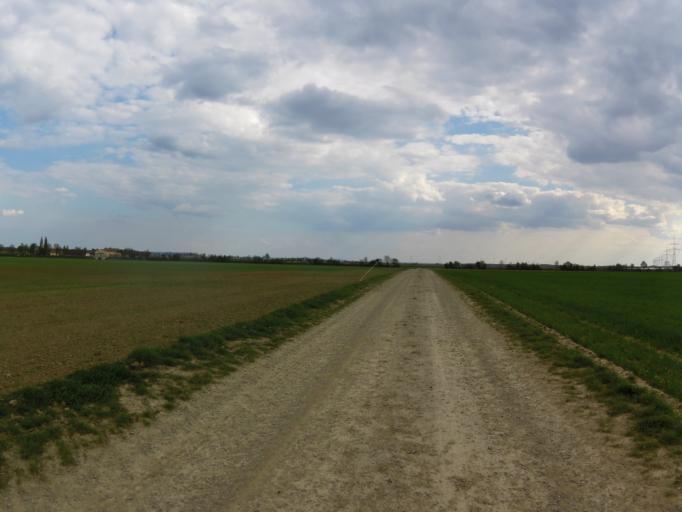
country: DE
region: Bavaria
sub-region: Regierungsbezirk Unterfranken
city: Oberpleichfeld
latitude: 49.8475
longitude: 10.0959
